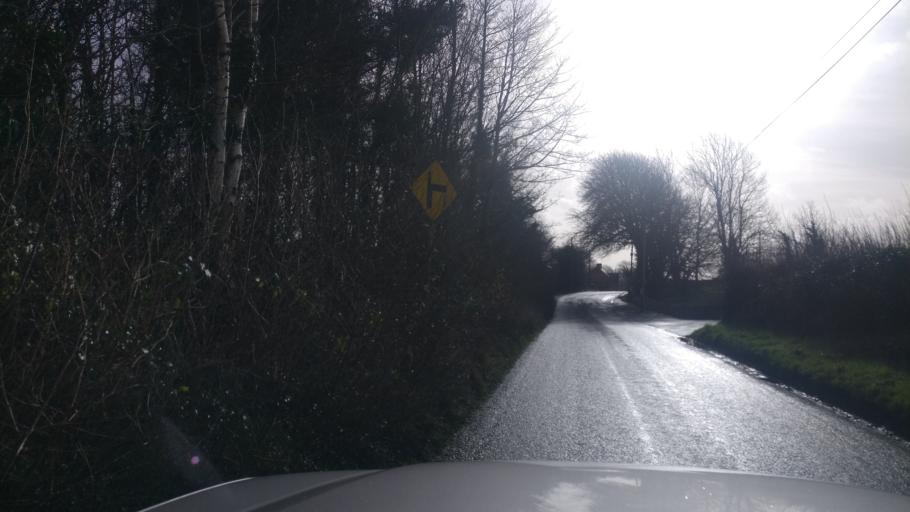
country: IE
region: Connaught
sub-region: County Galway
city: Loughrea
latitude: 53.2792
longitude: -8.5828
